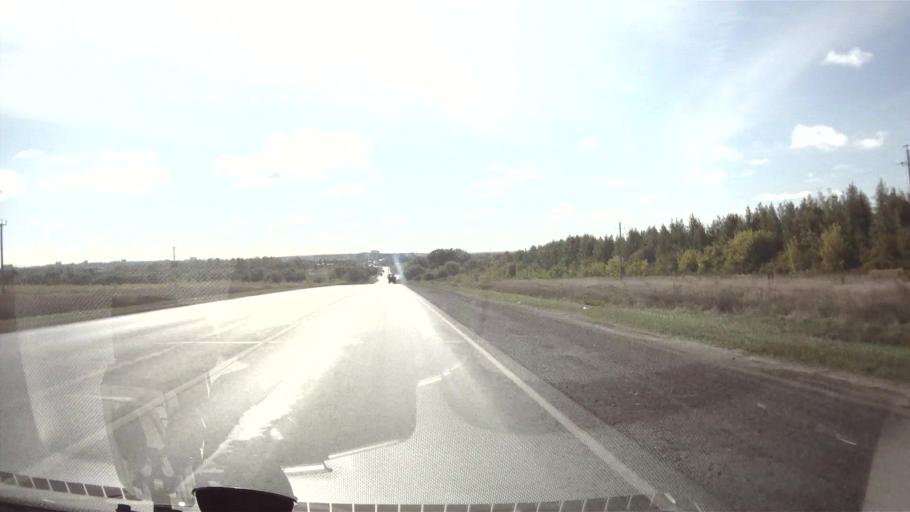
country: RU
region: Ulyanovsk
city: Isheyevka
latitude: 54.3097
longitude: 48.2373
